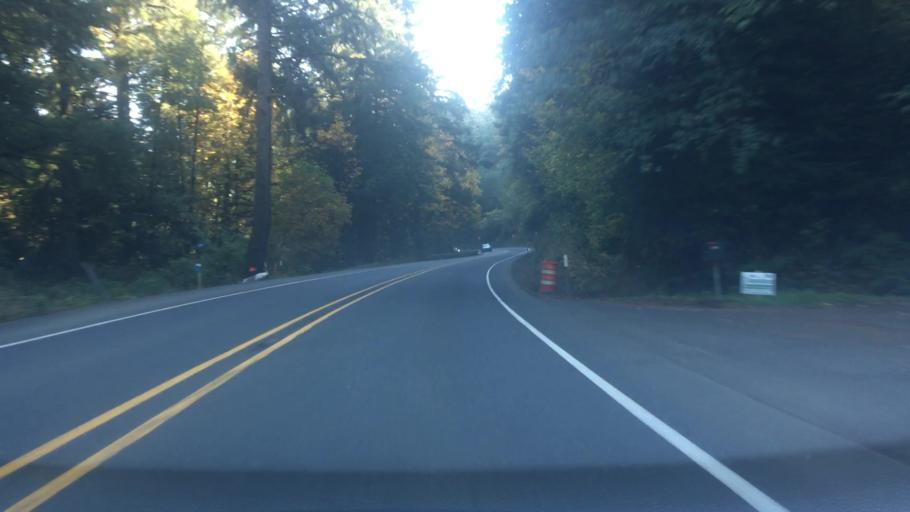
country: US
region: Oregon
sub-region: Lincoln County
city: Rose Lodge
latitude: 45.0082
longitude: -123.9197
